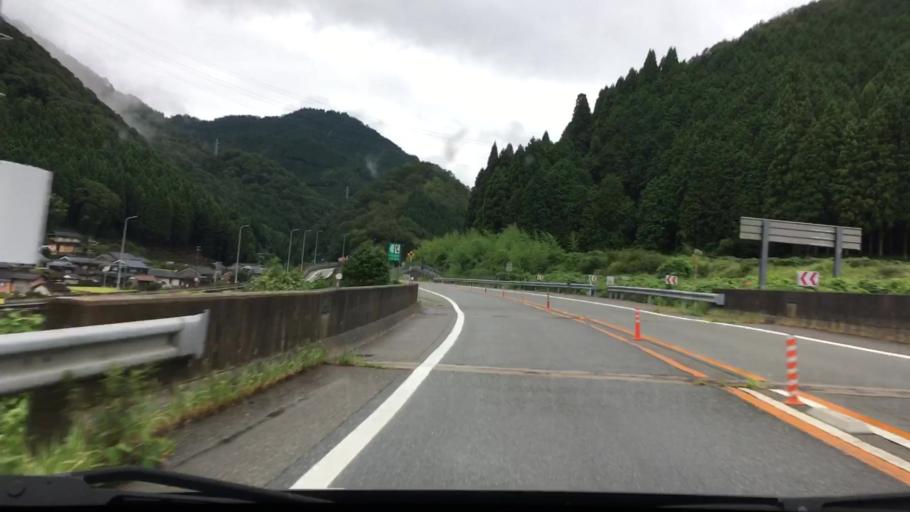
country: JP
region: Hyogo
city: Nishiwaki
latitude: 35.1896
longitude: 134.7908
